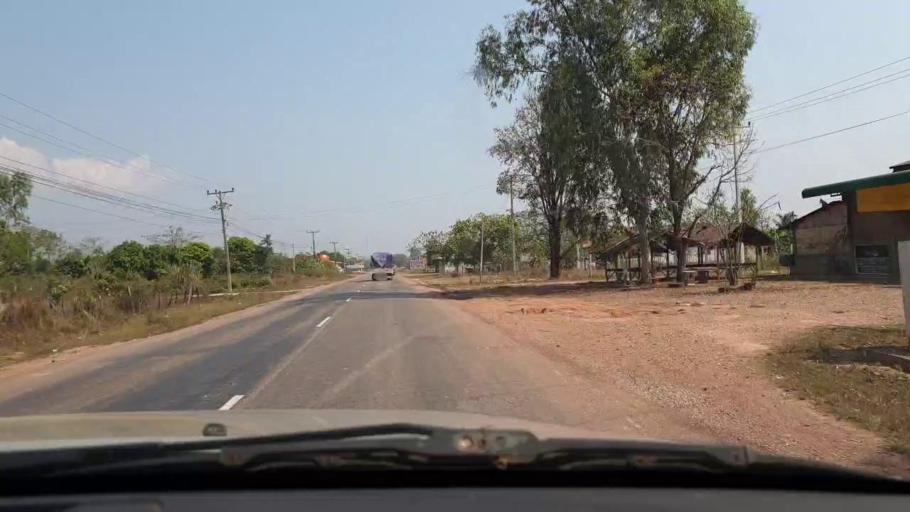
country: TH
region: Nong Khai
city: Phon Phisai
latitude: 18.1161
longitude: 103.0286
